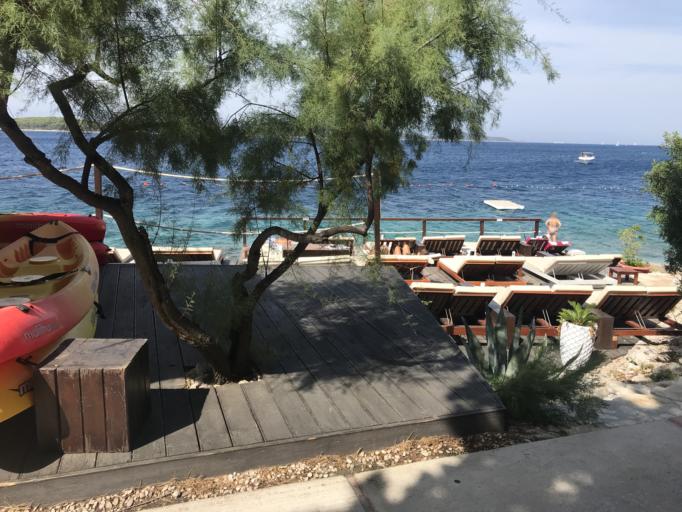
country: HR
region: Splitsko-Dalmatinska
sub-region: Grad Hvar
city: Hvar
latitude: 43.1712
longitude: 16.4315
